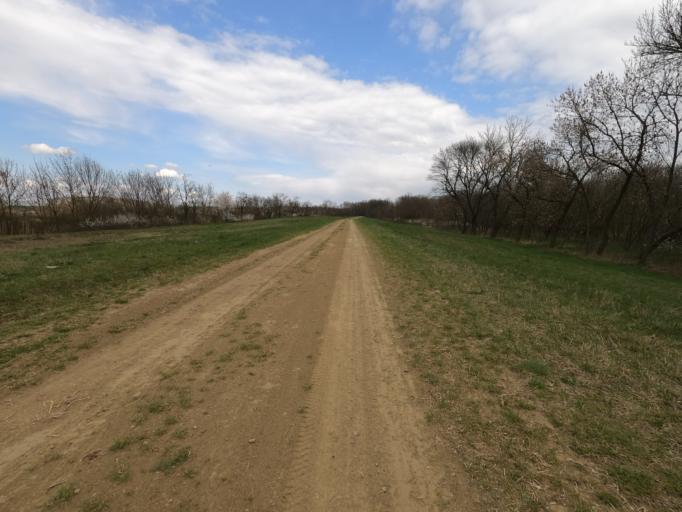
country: HU
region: Jasz-Nagykun-Szolnok
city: Turkeve
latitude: 47.0829
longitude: 20.7616
